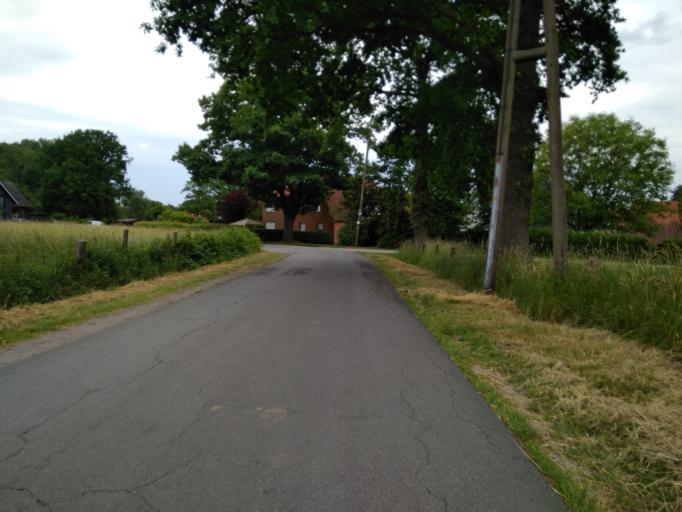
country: DE
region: North Rhine-Westphalia
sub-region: Regierungsbezirk Dusseldorf
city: Schermbeck
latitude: 51.6675
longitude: 6.8639
